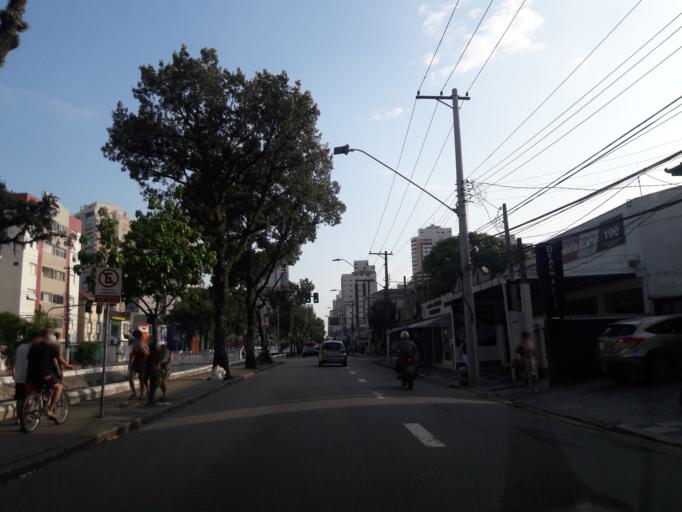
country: BR
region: Sao Paulo
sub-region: Santos
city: Santos
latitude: -23.9598
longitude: -46.3382
